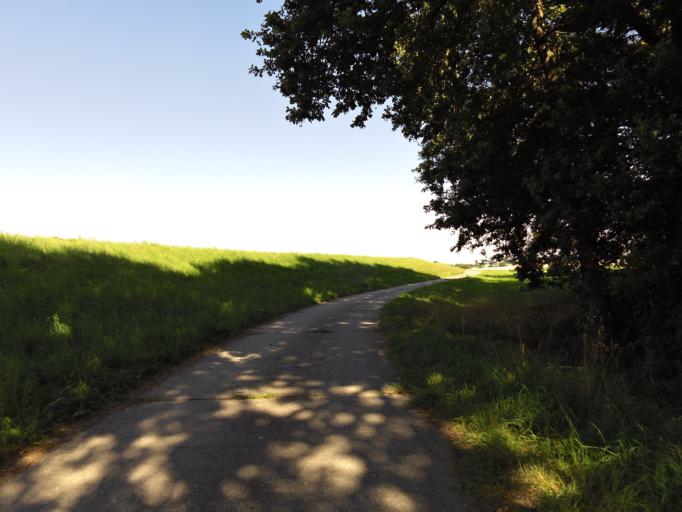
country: DE
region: Rheinland-Pfalz
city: Oppenheim
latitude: 49.8334
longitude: 8.4154
